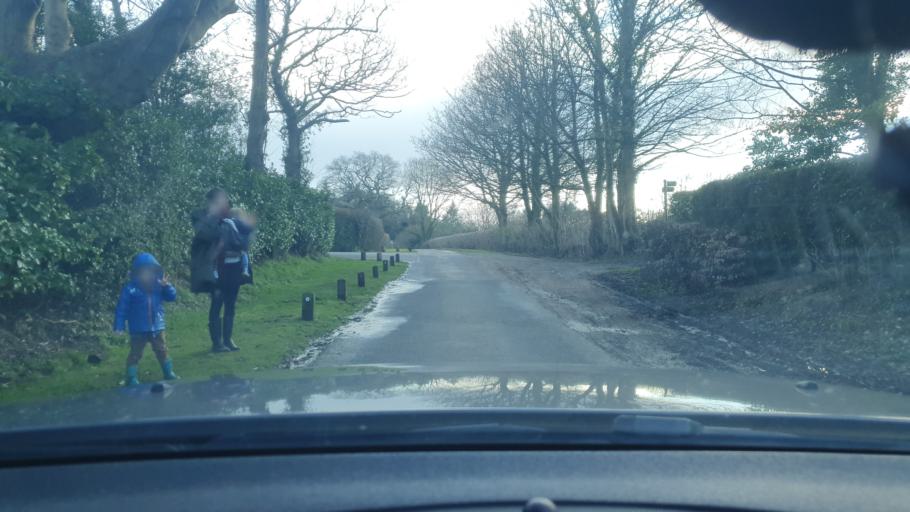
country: GB
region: England
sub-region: Wokingham
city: Wargrave
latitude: 51.5192
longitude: -0.8458
